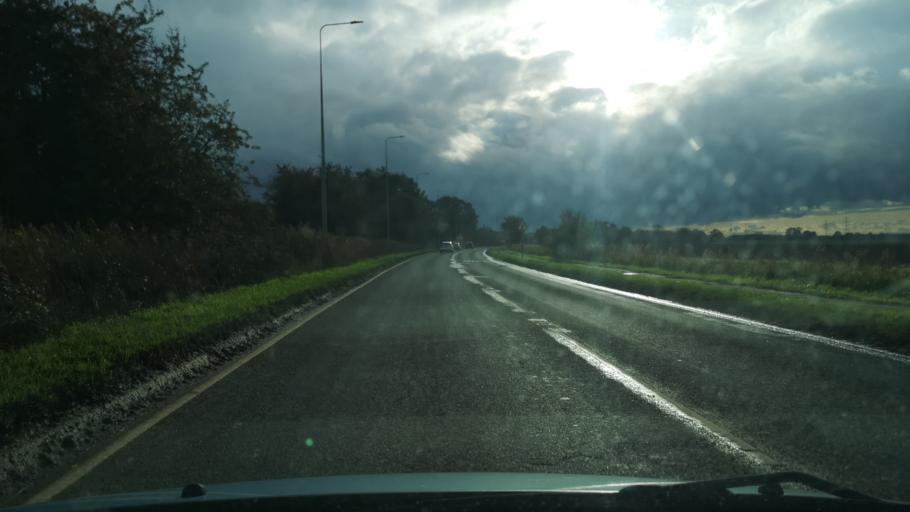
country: GB
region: England
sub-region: North Lincolnshire
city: Gunness
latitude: 53.5817
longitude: -0.7386
